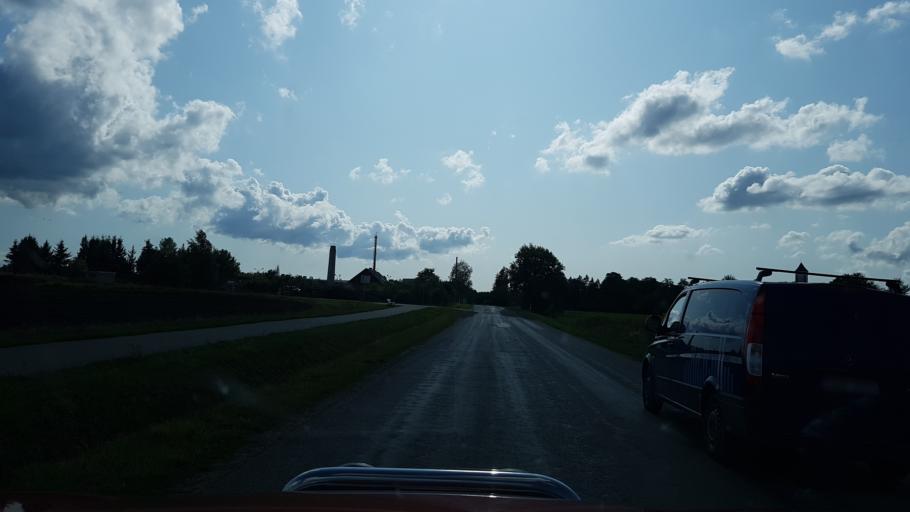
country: EE
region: Harju
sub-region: Paldiski linn
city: Paldiski
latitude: 59.2313
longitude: 24.0065
